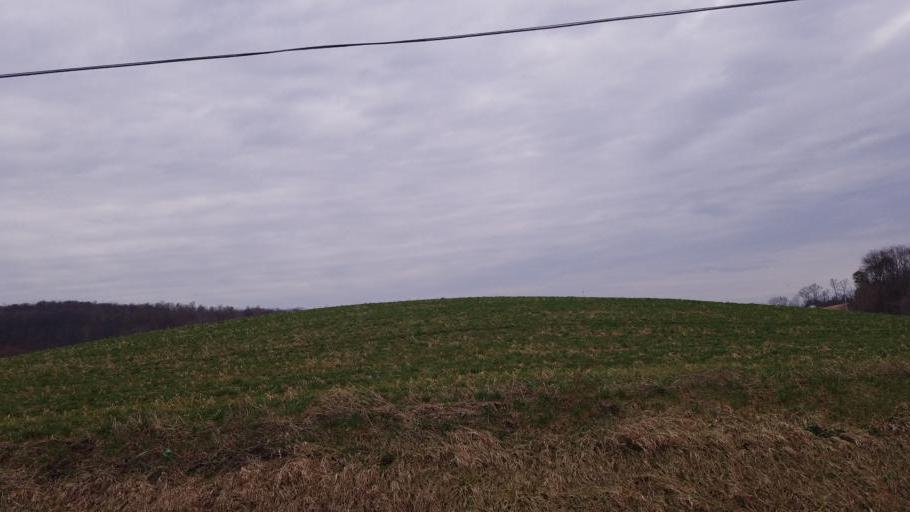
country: US
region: Ohio
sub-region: Sandusky County
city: Bellville
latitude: 40.5786
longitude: -82.4093
